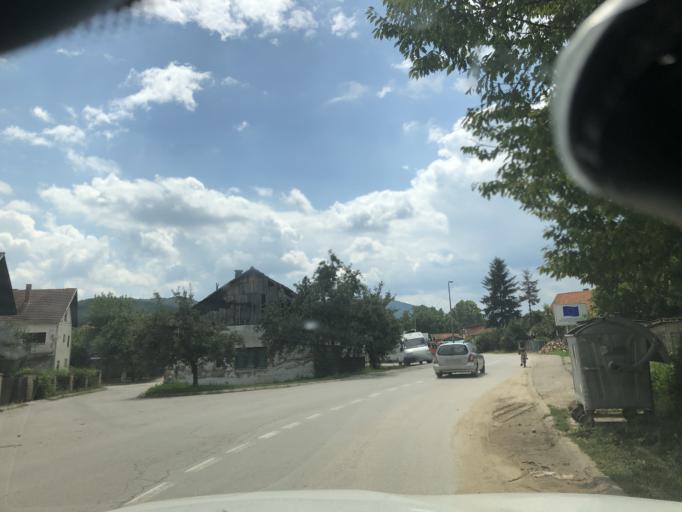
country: RS
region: Central Serbia
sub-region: Jablanicki Okrug
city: Medvega
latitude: 42.8456
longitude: 21.5869
